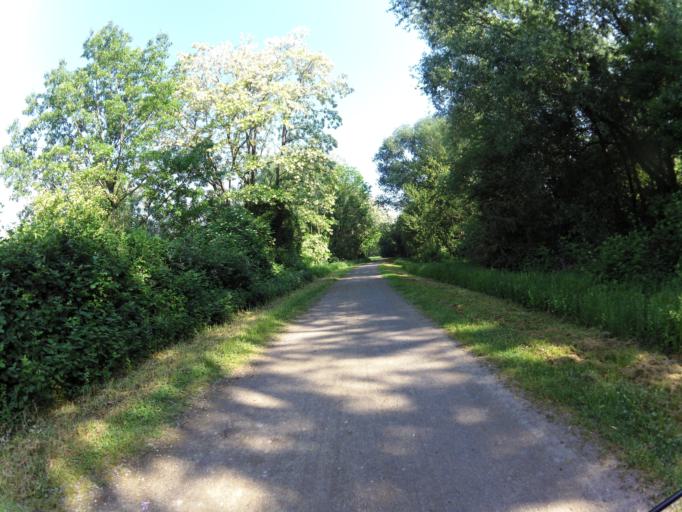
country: DE
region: North Rhine-Westphalia
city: Julich
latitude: 50.9453
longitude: 6.3244
